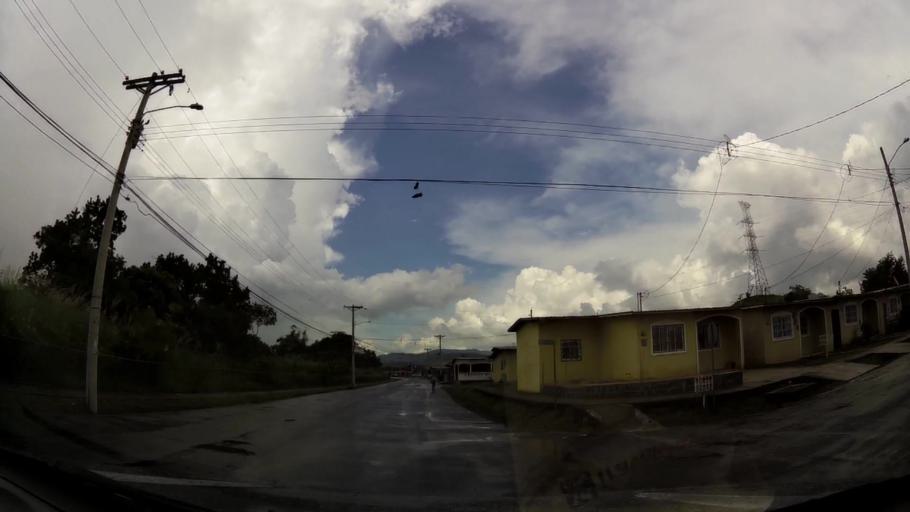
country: PA
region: Panama
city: Cabra Numero Uno
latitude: 9.1144
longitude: -79.3384
